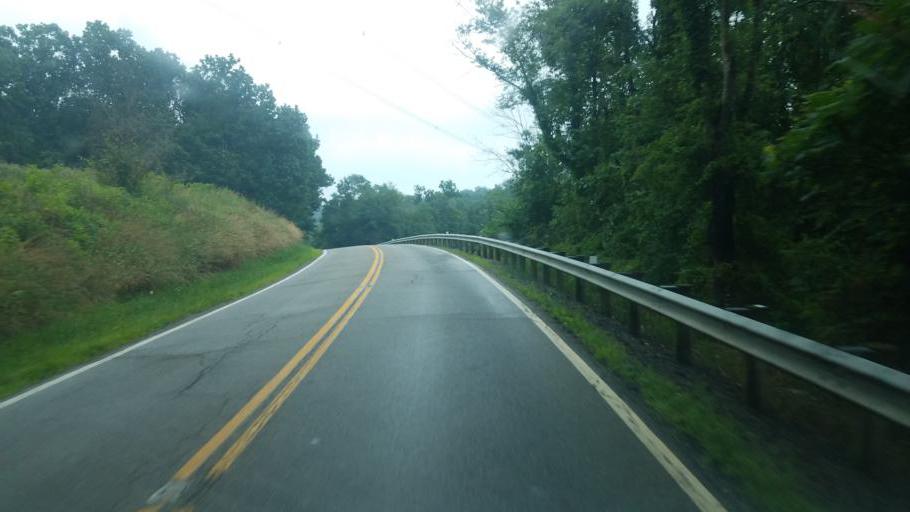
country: US
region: Ohio
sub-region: Carroll County
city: Carrollton
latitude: 40.4646
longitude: -80.9932
